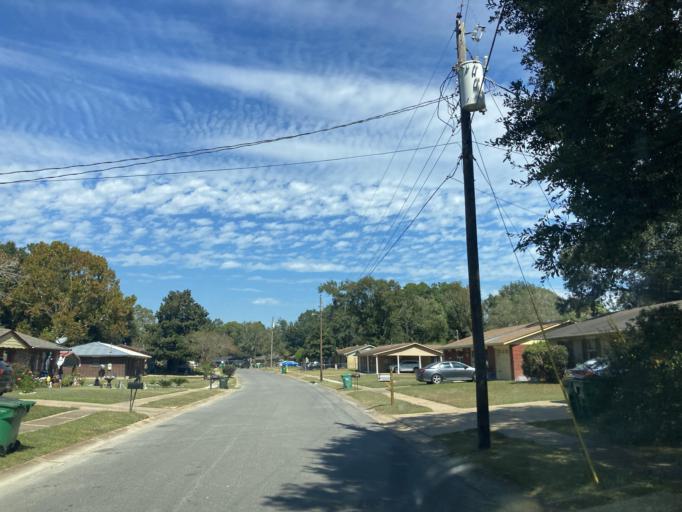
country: US
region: Mississippi
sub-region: Jackson County
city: Saint Martin
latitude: 30.4512
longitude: -88.8751
